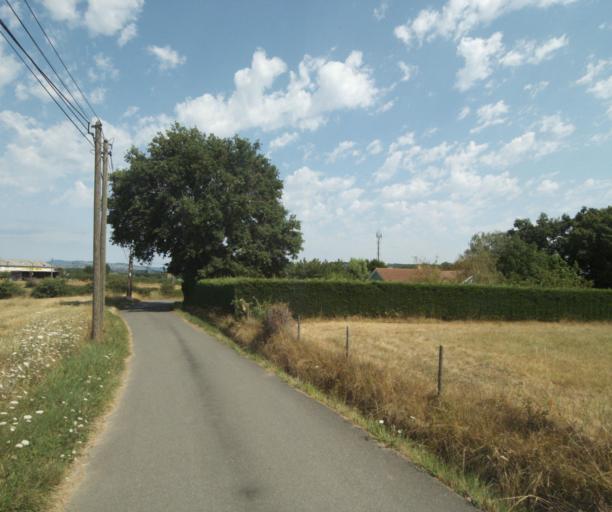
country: FR
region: Rhone-Alpes
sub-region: Departement du Rhone
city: Lentilly
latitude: 45.8488
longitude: 4.6537
